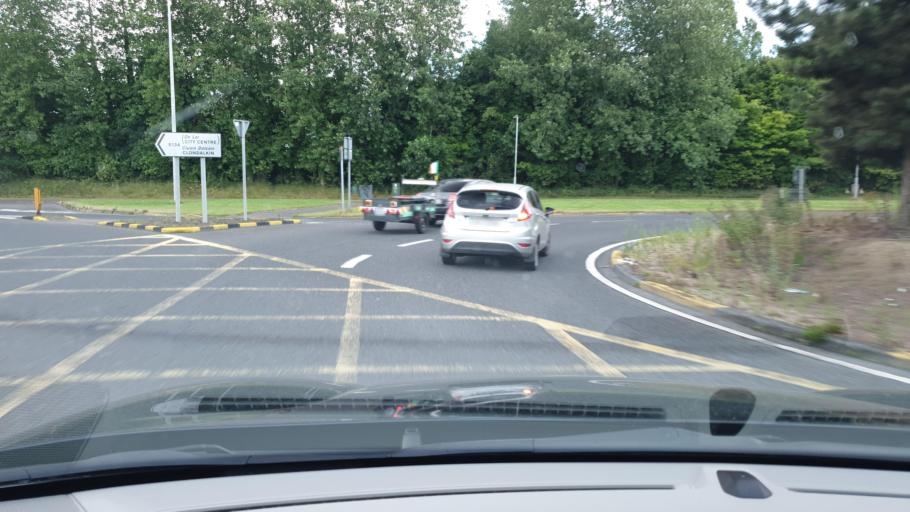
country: IE
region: Leinster
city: Clondalkin
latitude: 53.3248
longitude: -6.4049
